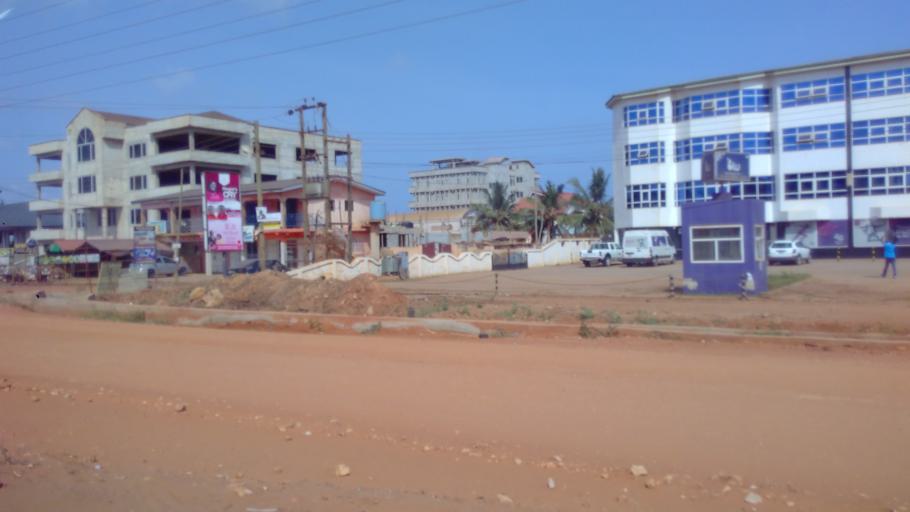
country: GH
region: Greater Accra
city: Nungua
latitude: 5.6300
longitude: -0.0664
